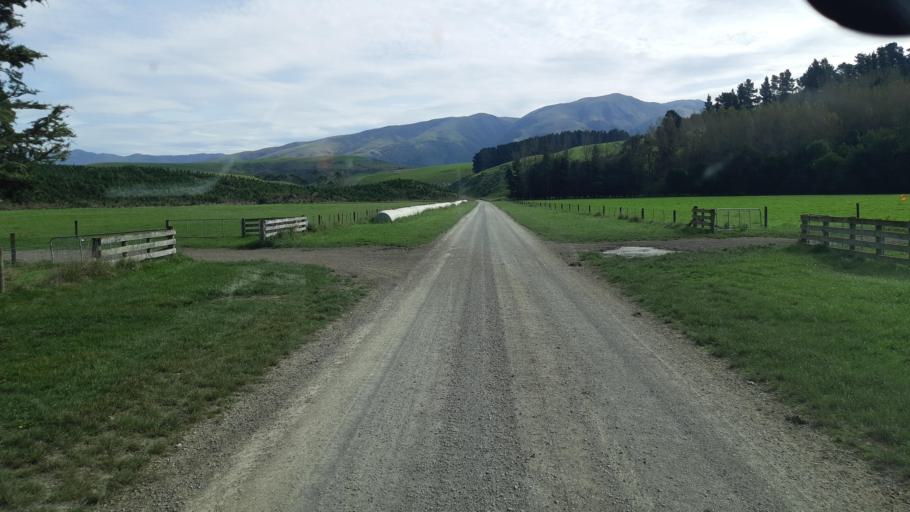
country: NZ
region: Canterbury
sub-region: Timaru District
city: Pleasant Point
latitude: -44.1876
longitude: 170.8012
